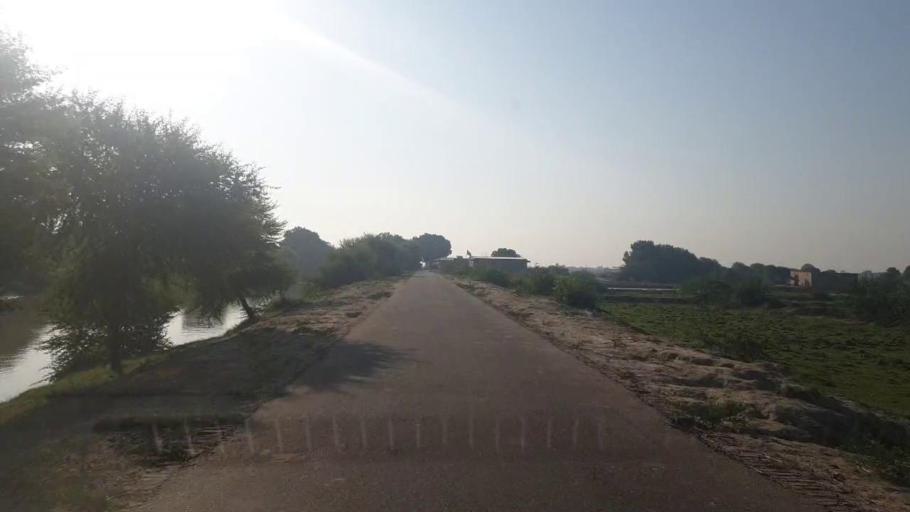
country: PK
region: Sindh
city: Tando Bago
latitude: 24.7221
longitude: 68.9397
